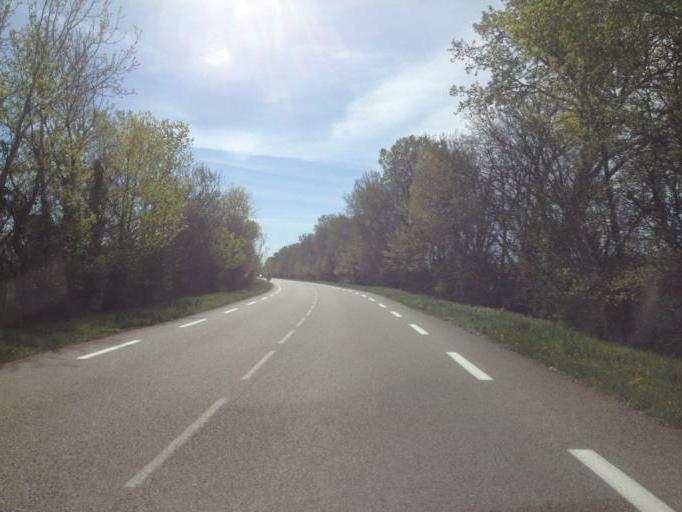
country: FR
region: Provence-Alpes-Cote d'Azur
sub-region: Departement du Vaucluse
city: Caderousse
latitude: 44.1165
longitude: 4.7217
